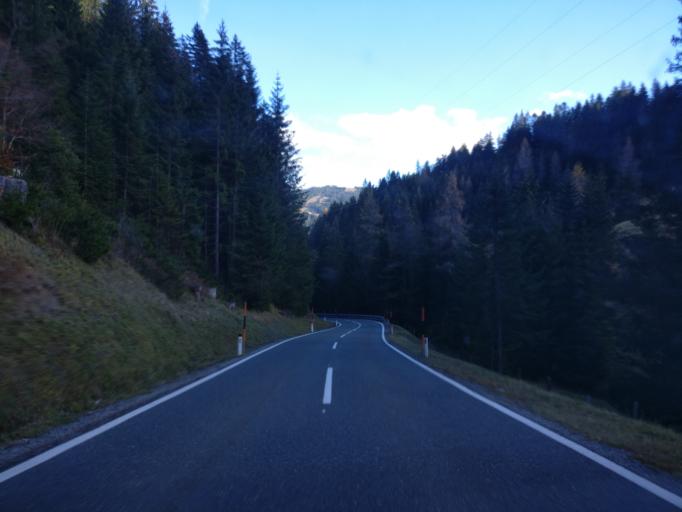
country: AT
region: Salzburg
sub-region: Politischer Bezirk Zell am See
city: Dienten am Hochkonig
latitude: 47.3964
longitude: 13.0076
